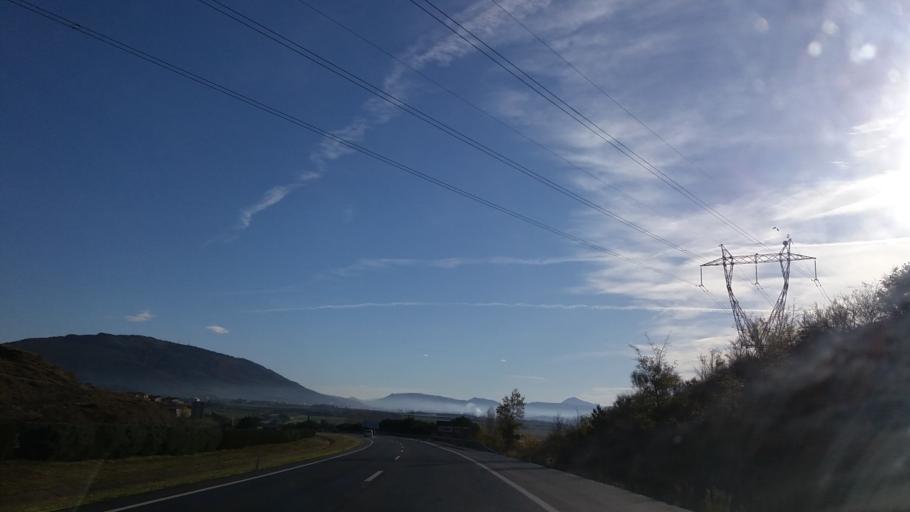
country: ES
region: Navarre
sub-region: Provincia de Navarra
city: Oltza
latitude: 42.8569
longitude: -1.7385
